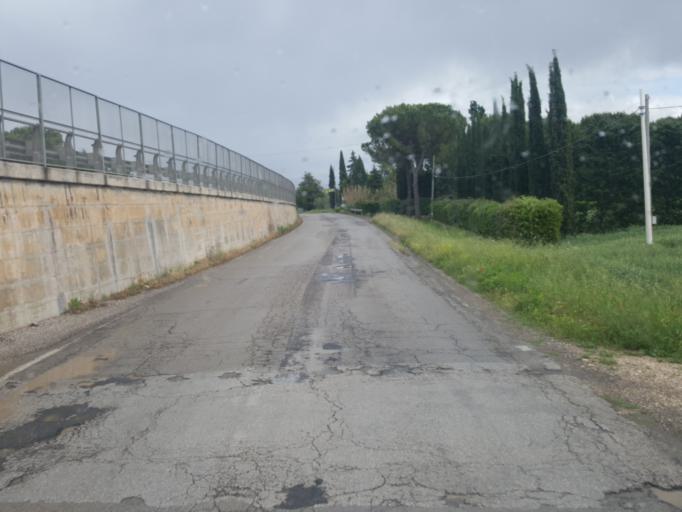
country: IT
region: Umbria
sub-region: Provincia di Perugia
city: Via Lippia
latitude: 43.0824
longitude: 12.4889
